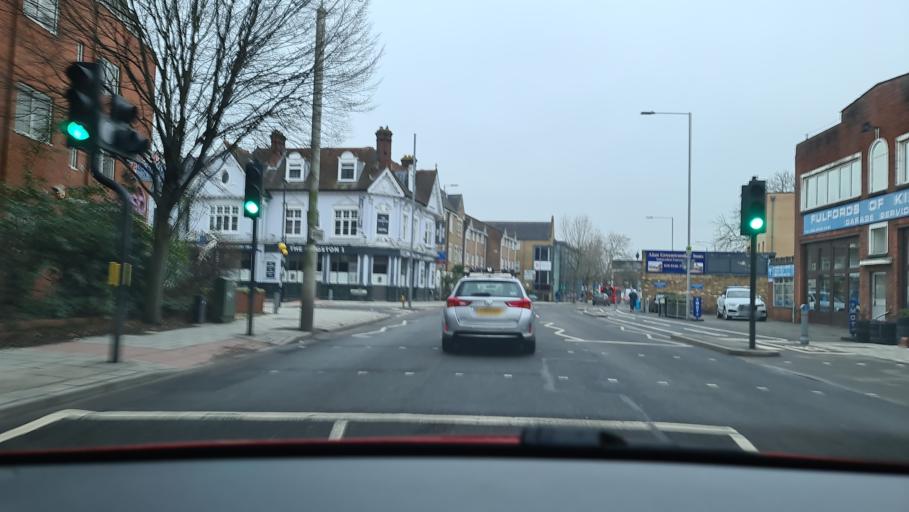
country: GB
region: England
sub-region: Greater London
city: Kingston upon Thames
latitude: 51.4106
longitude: -0.2941
